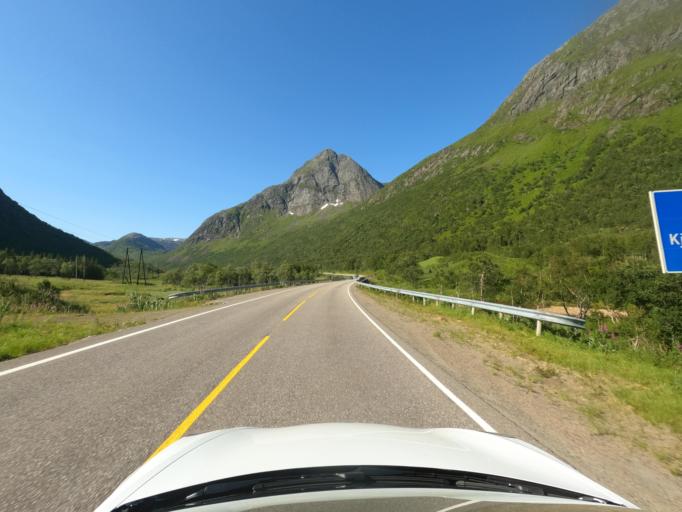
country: NO
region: Nordland
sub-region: Lodingen
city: Lodingen
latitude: 68.5072
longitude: 15.7238
